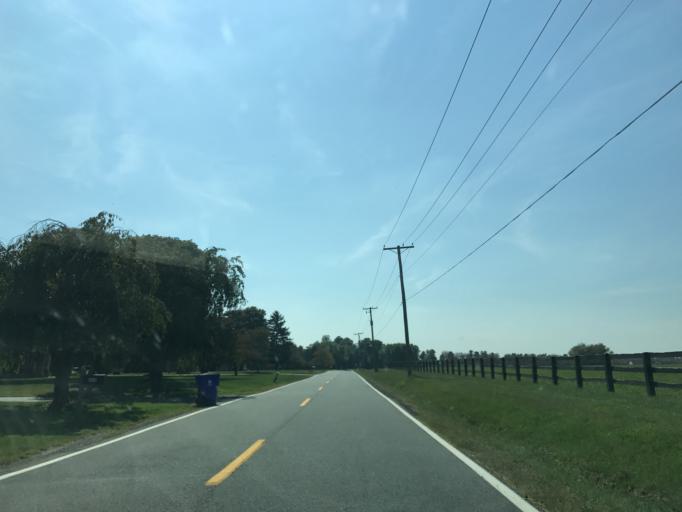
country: US
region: Delaware
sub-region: New Castle County
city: Middletown
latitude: 39.4990
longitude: -75.8062
